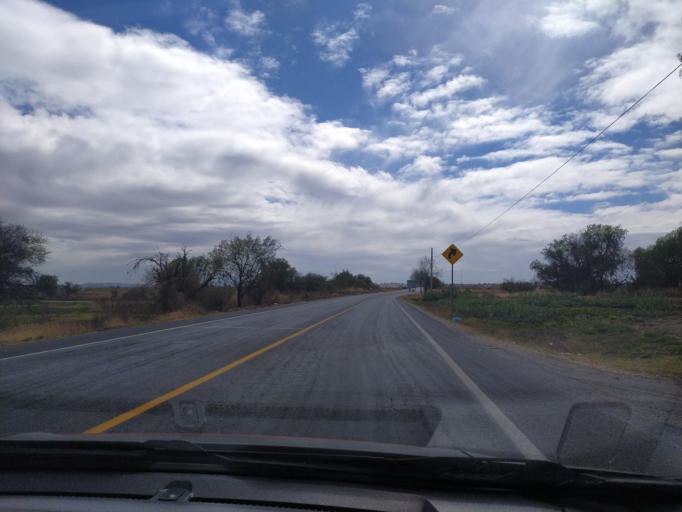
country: LA
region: Oudomxai
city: Muang La
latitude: 21.0140
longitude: 101.8280
